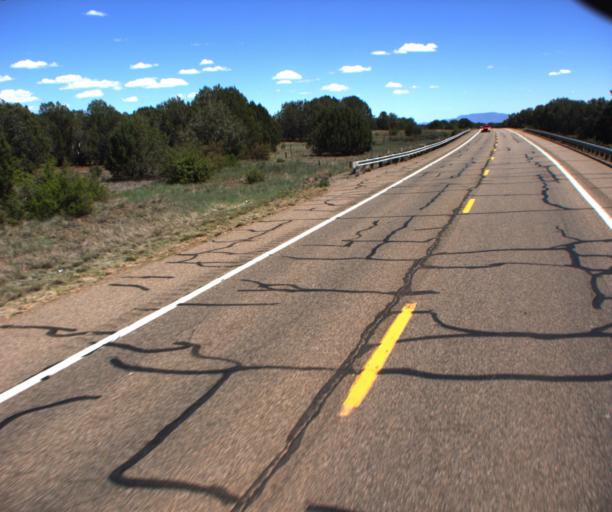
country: US
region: Arizona
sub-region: Yavapai County
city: Paulden
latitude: 35.1067
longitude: -112.4289
